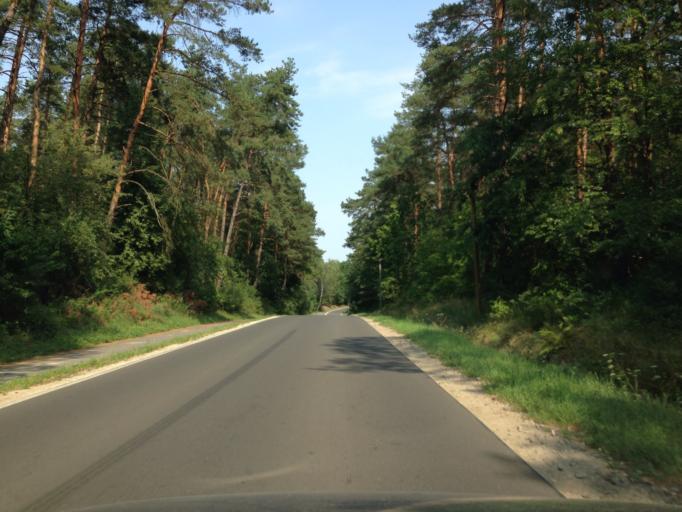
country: PL
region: Kujawsko-Pomorskie
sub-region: Powiat golubsko-dobrzynski
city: Golub-Dobrzyn
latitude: 53.0888
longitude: 19.0358
